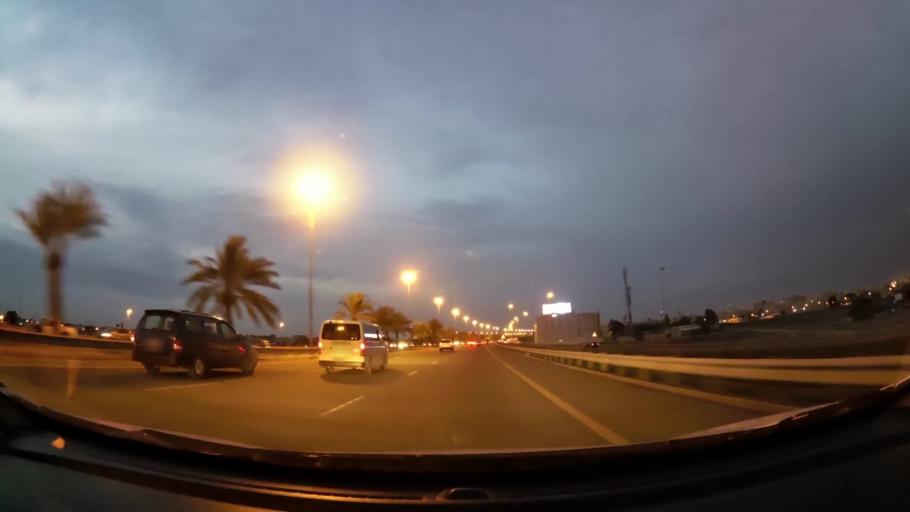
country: BH
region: Northern
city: Madinat `Isa
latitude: 26.1893
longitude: 50.5044
